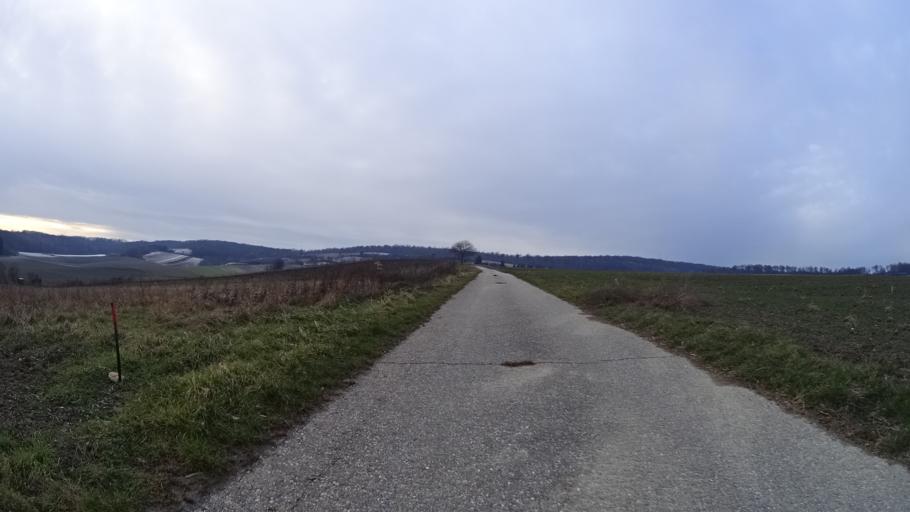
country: AT
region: Lower Austria
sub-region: Politischer Bezirk Korneuburg
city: Harmannsdorf
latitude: 48.4015
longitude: 16.3440
